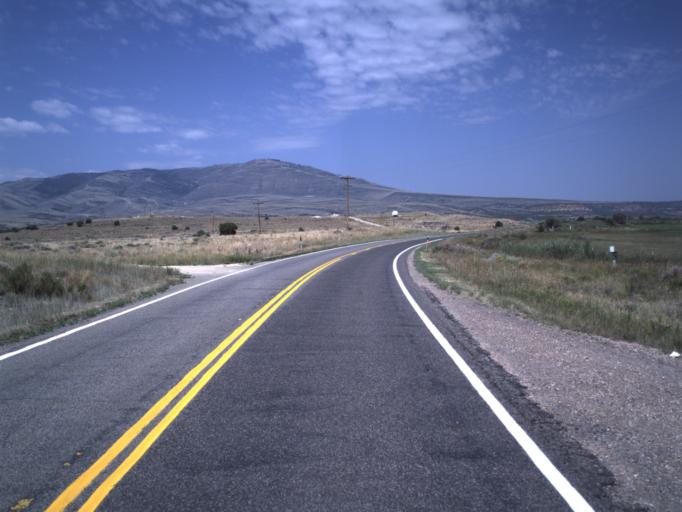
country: US
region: Utah
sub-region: Daggett County
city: Manila
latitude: 40.9779
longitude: -109.8015
